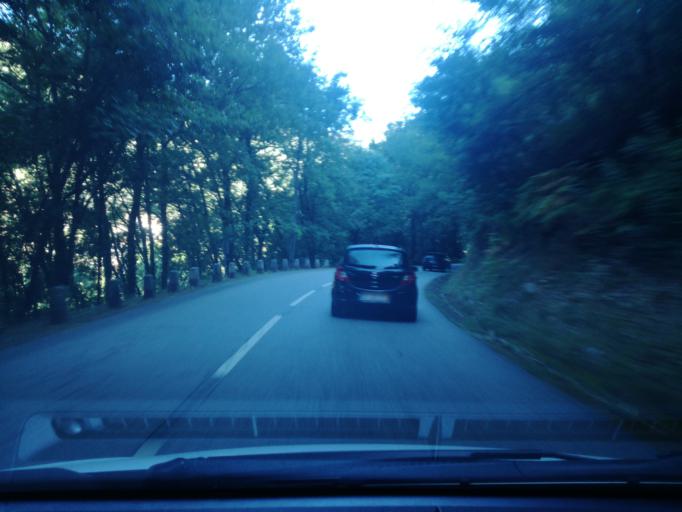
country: PT
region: Braga
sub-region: Vieira do Minho
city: Real
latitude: 41.7113
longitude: -8.1657
